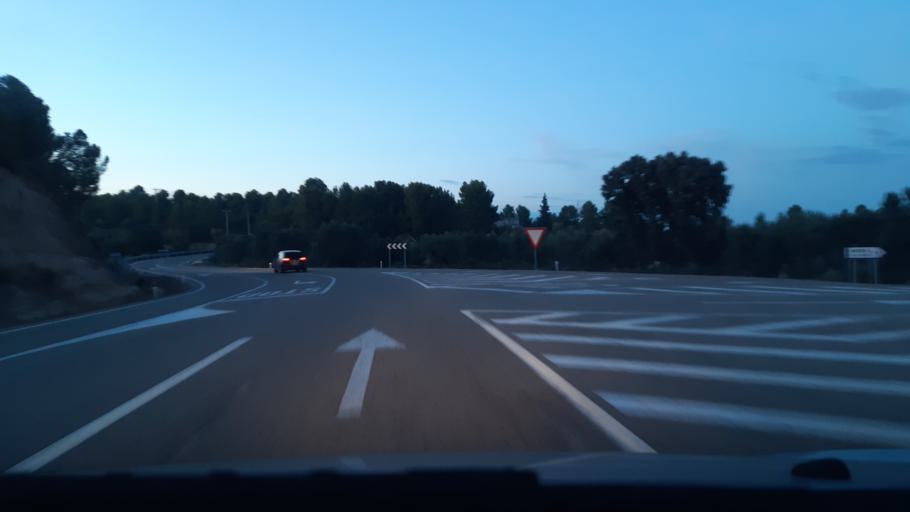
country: ES
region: Aragon
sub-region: Provincia de Teruel
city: Calaceite
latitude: 40.9783
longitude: 0.2024
